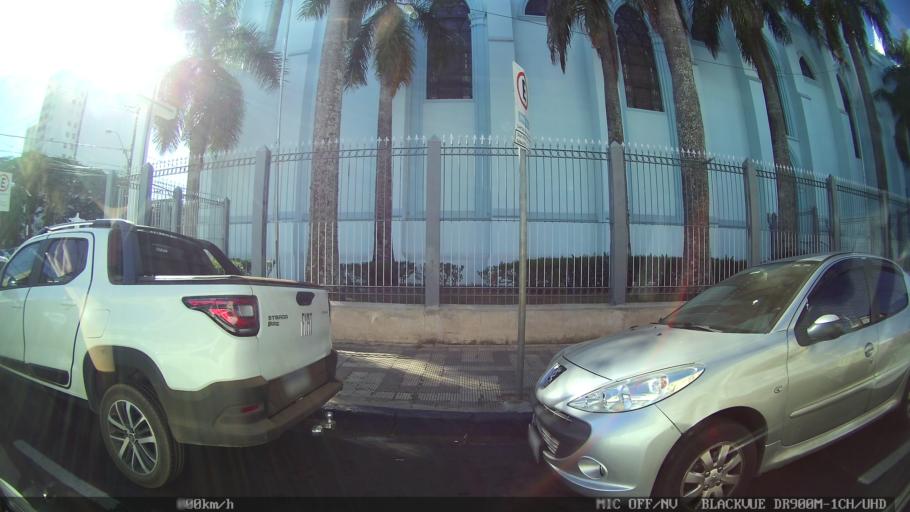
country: BR
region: Sao Paulo
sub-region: Franca
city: Franca
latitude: -20.5395
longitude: -47.4016
